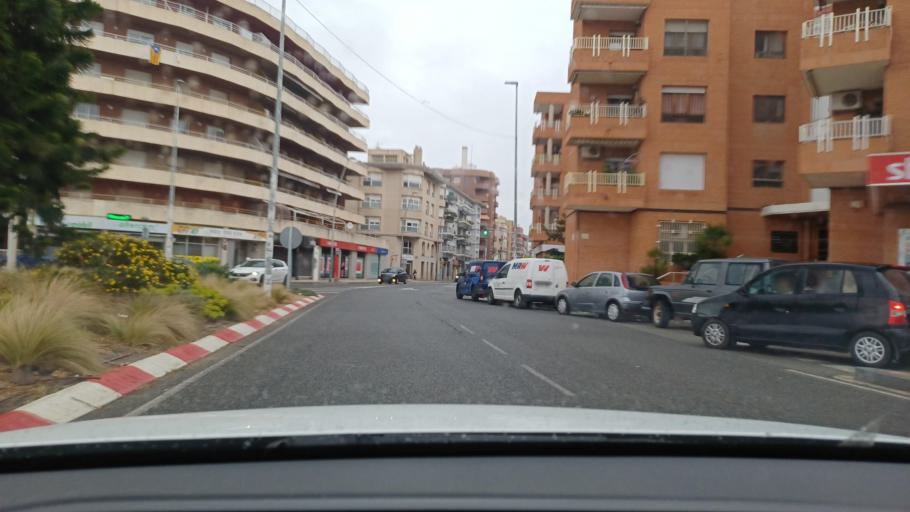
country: ES
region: Catalonia
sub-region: Provincia de Tarragona
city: Tortosa
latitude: 40.8024
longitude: 0.5204
